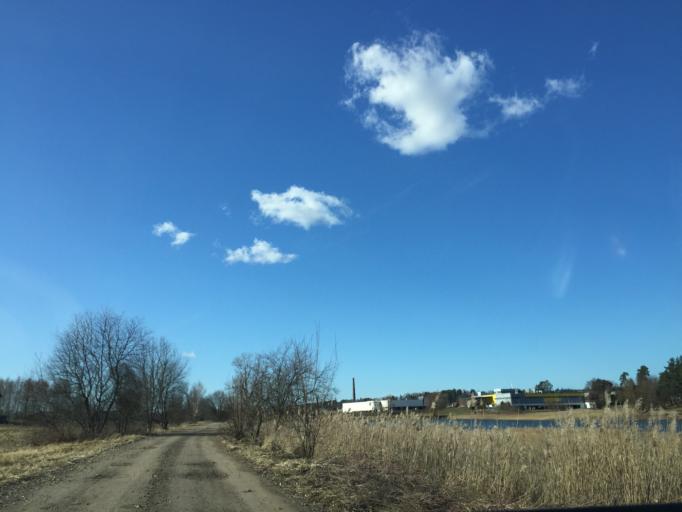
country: LV
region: Ogre
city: Ogre
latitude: 56.8123
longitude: 24.5920
